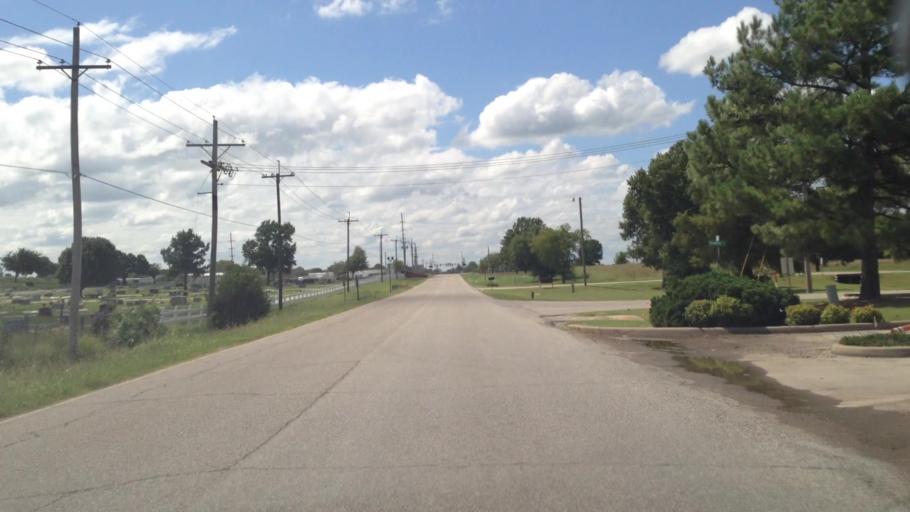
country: US
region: Oklahoma
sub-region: Craig County
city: Vinita
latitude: 36.6560
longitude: -95.1387
